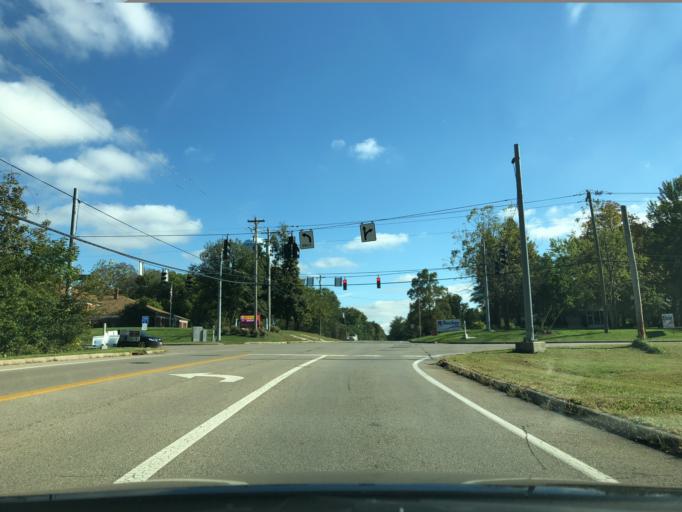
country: US
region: Ohio
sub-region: Hamilton County
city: Loveland
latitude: 39.2375
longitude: -84.2659
